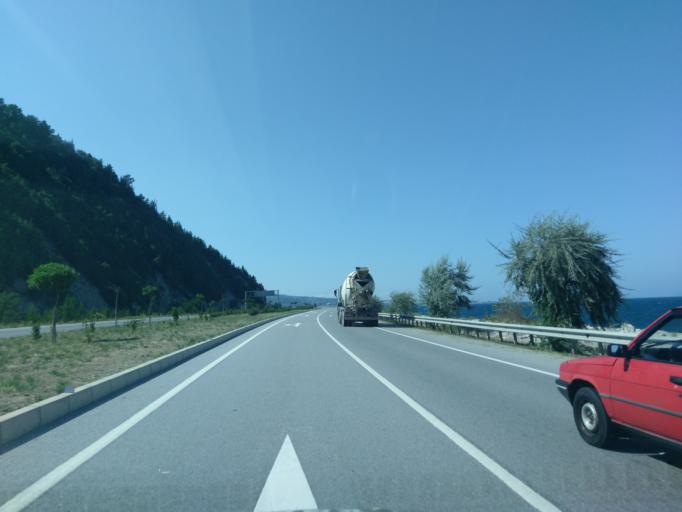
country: TR
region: Sinop
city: Gerze
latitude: 41.7477
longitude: 35.2429
